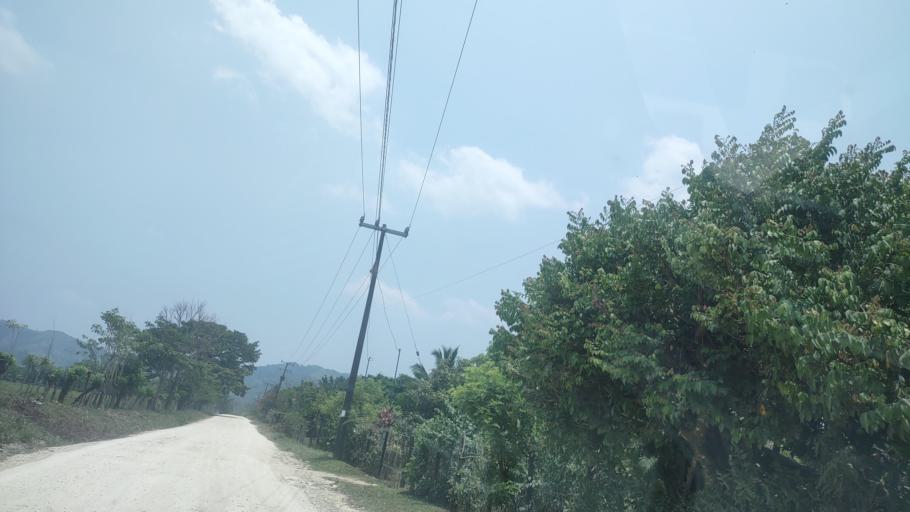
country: MX
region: Chiapas
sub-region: Tecpatan
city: Raudales Malpaso
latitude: 17.4591
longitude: -93.8045
